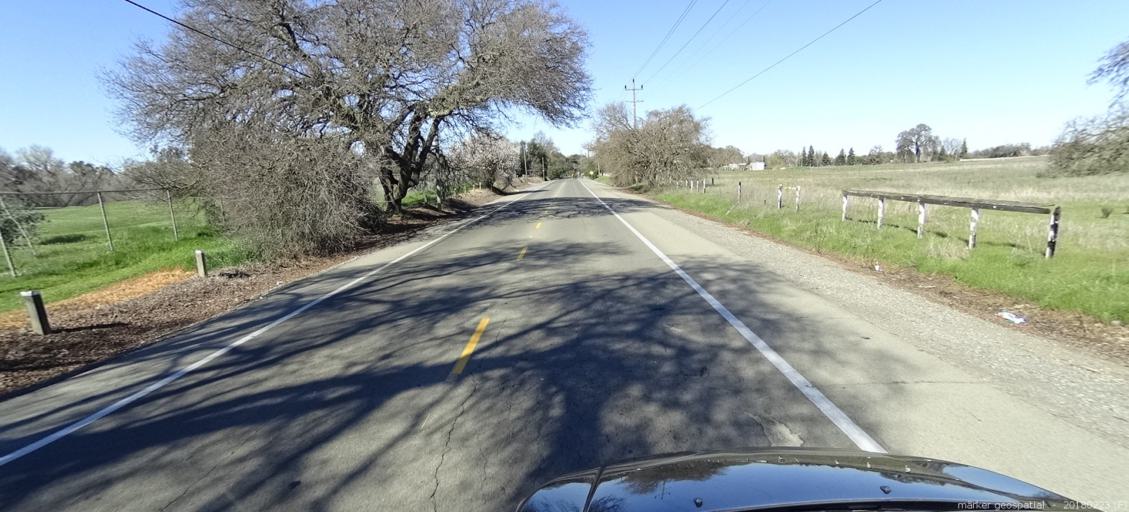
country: US
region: California
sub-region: Sacramento County
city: North Highlands
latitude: 38.7109
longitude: -121.4016
